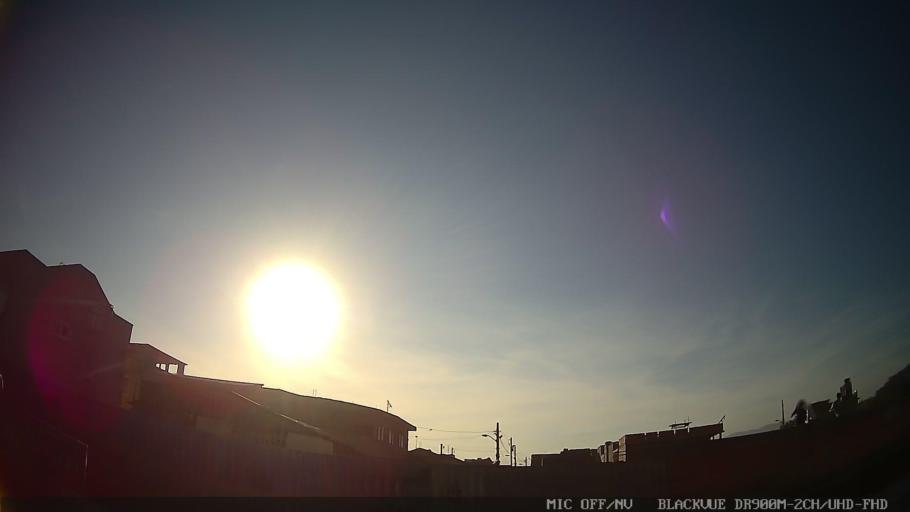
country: BR
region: Sao Paulo
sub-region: Guaruja
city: Guaruja
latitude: -23.9683
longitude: -46.2445
